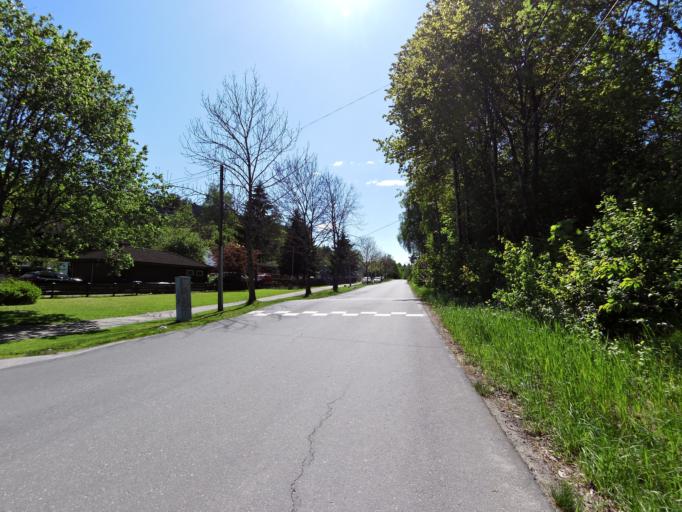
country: NO
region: Ostfold
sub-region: Fredrikstad
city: Fredrikstad
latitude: 59.2274
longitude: 10.9680
